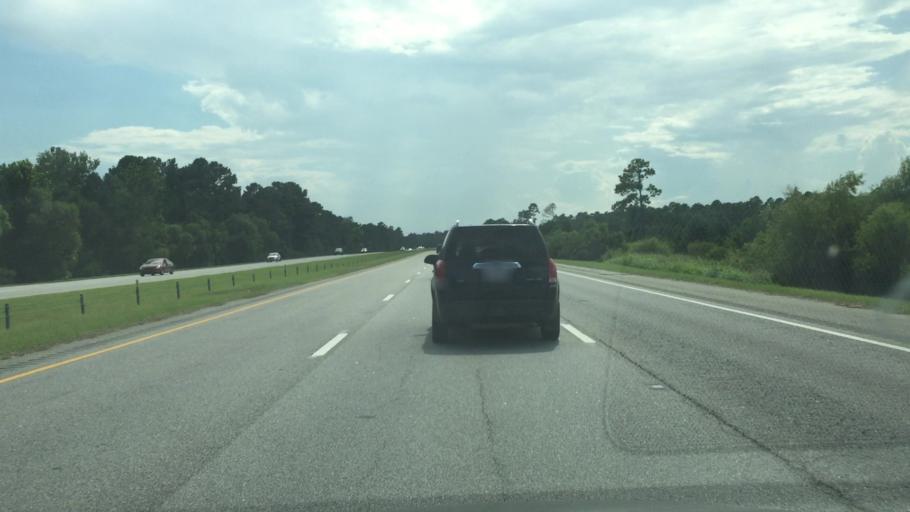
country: US
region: South Carolina
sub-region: Horry County
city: Myrtle Beach
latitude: 33.7699
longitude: -78.8256
